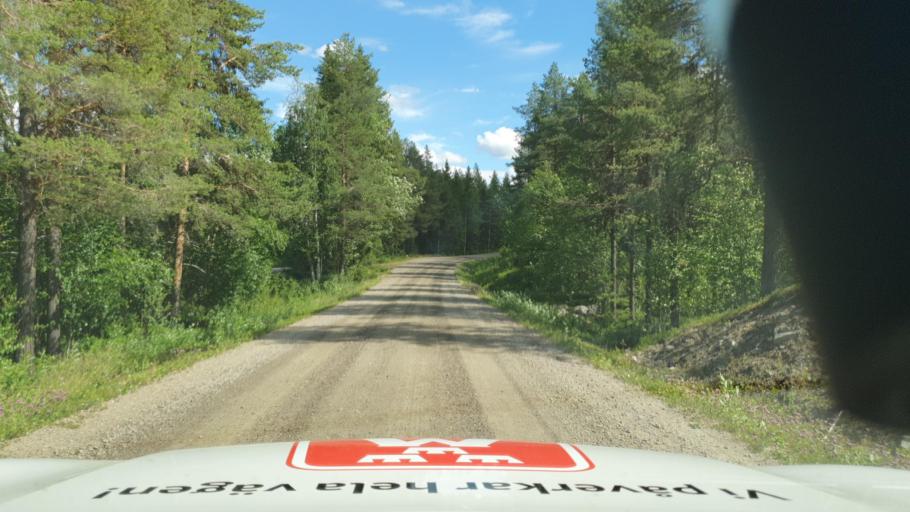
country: SE
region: Vaesterbotten
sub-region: Sorsele Kommun
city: Sorsele
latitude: 65.6713
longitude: 17.2835
